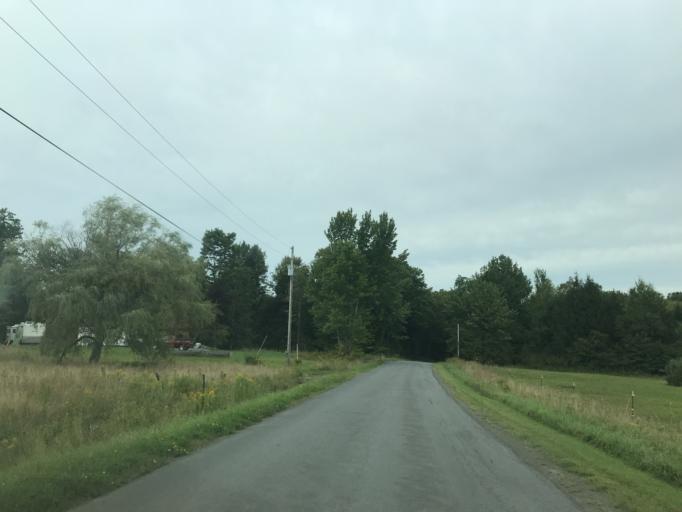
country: US
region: New York
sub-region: Otsego County
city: Worcester
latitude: 42.5858
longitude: -74.6767
